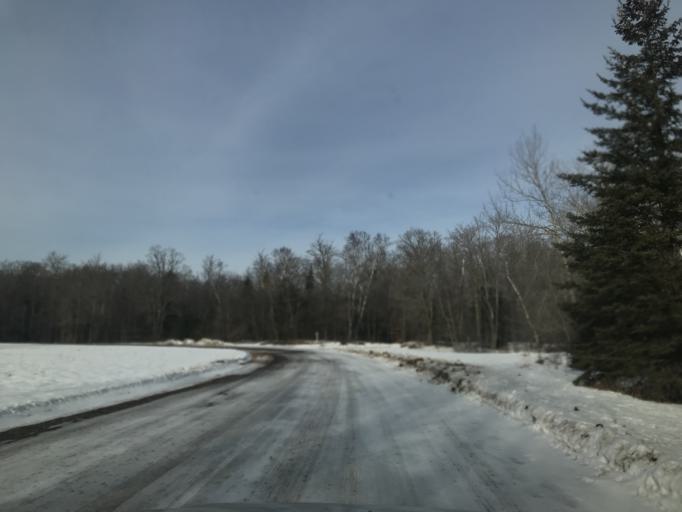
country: US
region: Wisconsin
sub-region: Door County
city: Sturgeon Bay
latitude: 45.1523
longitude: -87.0548
